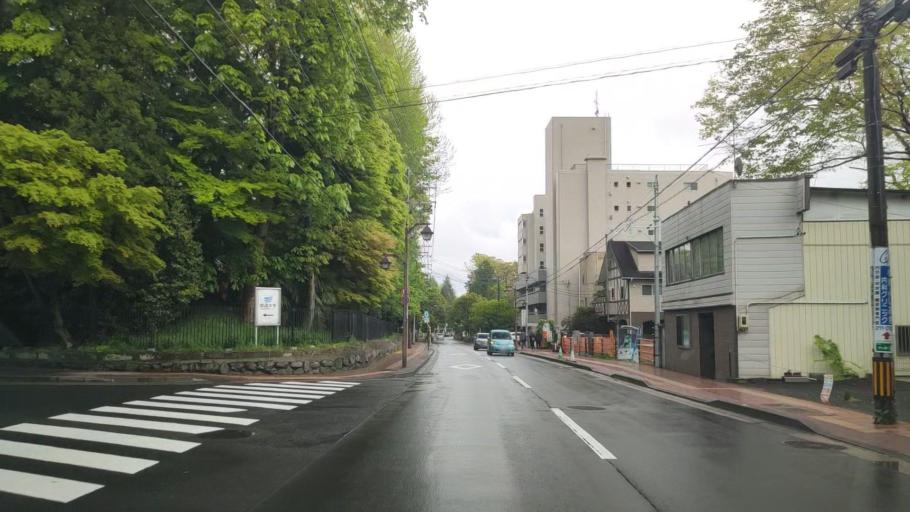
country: JP
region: Miyagi
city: Sendai
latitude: 38.2556
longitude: 140.8690
